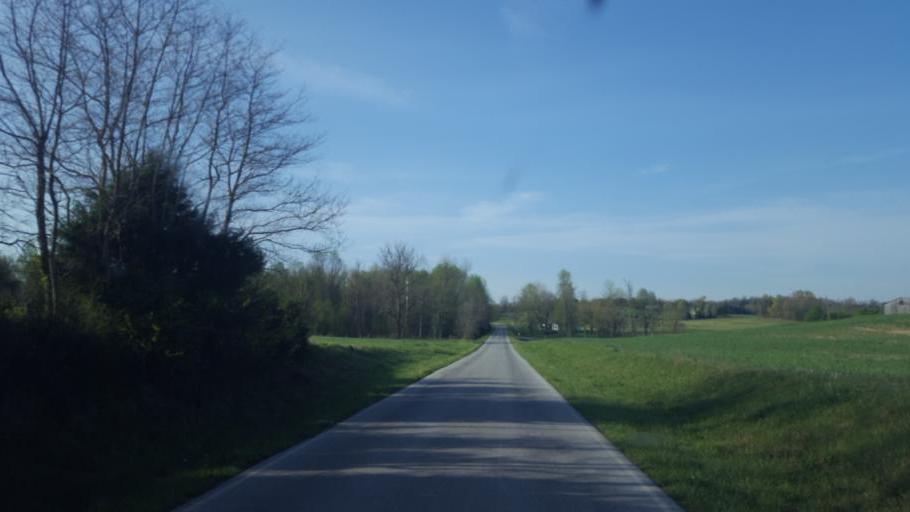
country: US
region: Kentucky
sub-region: Hardin County
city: Elizabethtown
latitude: 37.4931
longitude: -85.9615
